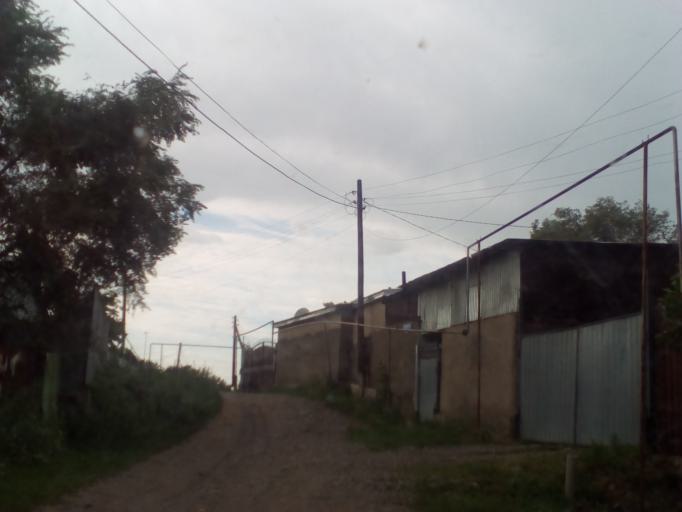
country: KZ
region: Almaty Oblysy
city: Burunday
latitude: 43.1567
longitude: 76.4058
